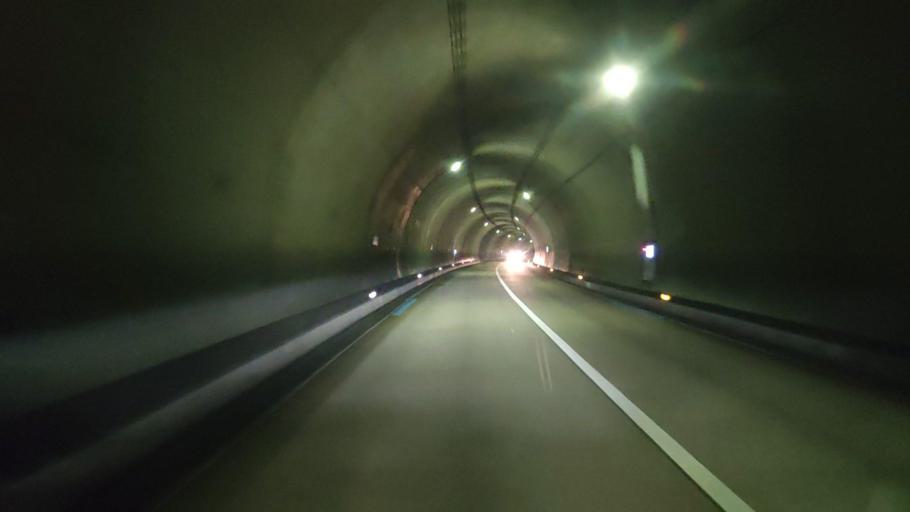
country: JP
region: Wakayama
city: Shingu
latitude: 33.8524
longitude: 135.8553
